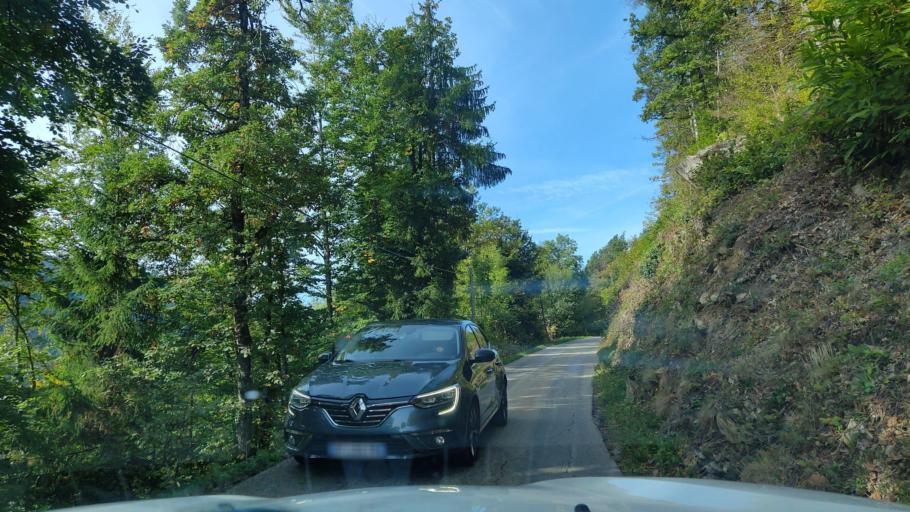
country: FR
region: Rhone-Alpes
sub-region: Departement de la Savoie
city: Beaufort
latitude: 45.7217
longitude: 6.5055
